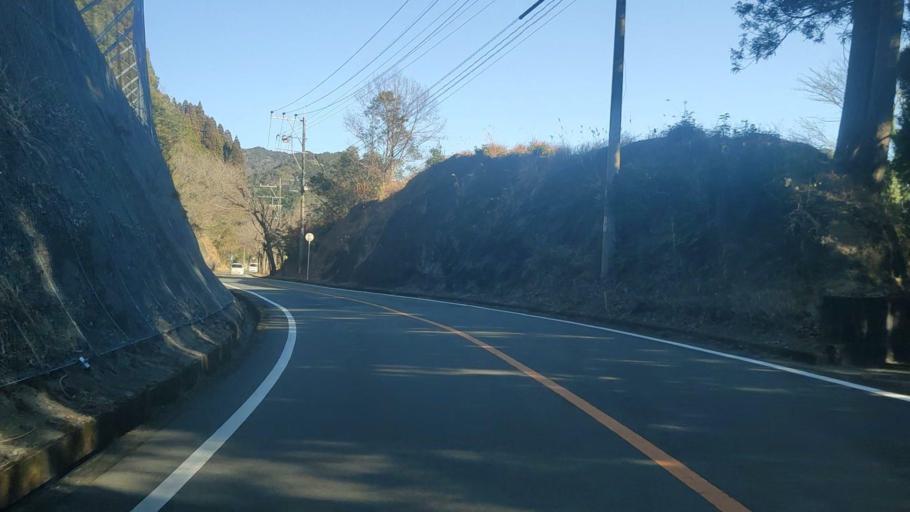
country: JP
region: Miyazaki
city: Nobeoka
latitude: 32.6403
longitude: 131.7442
